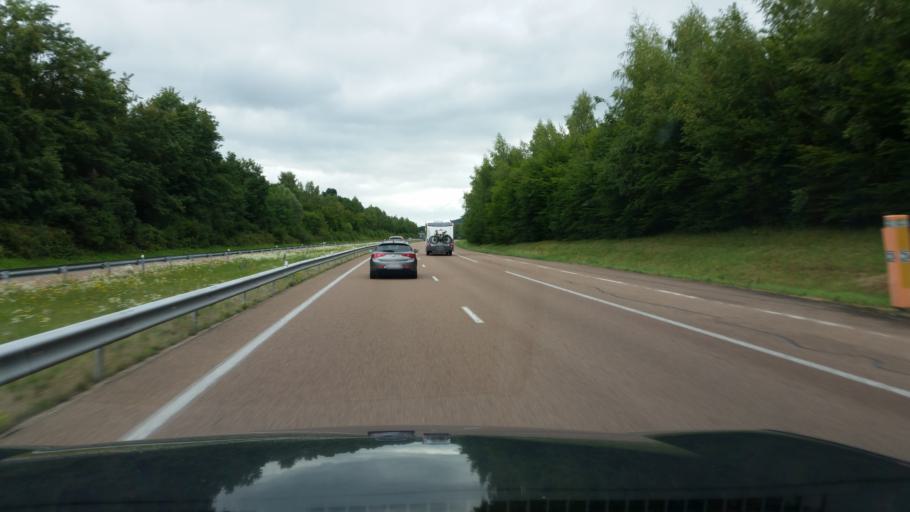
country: FR
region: Franche-Comte
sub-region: Departement du Jura
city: Bletterans
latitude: 46.7123
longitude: 5.4872
